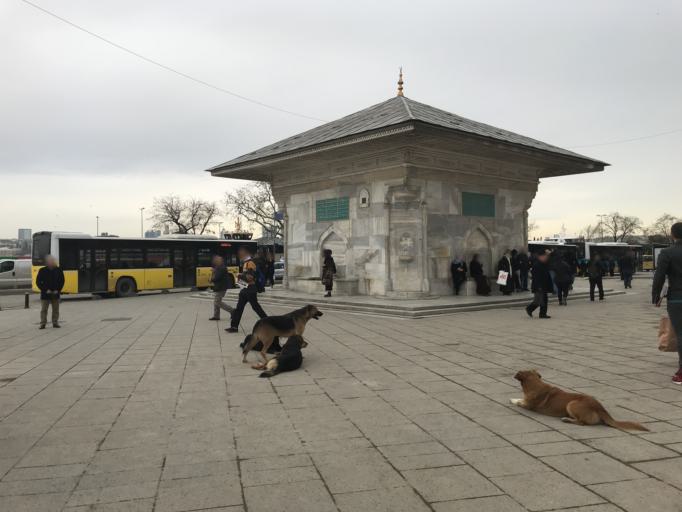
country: TR
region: Istanbul
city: UEskuedar
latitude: 41.0266
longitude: 29.0154
